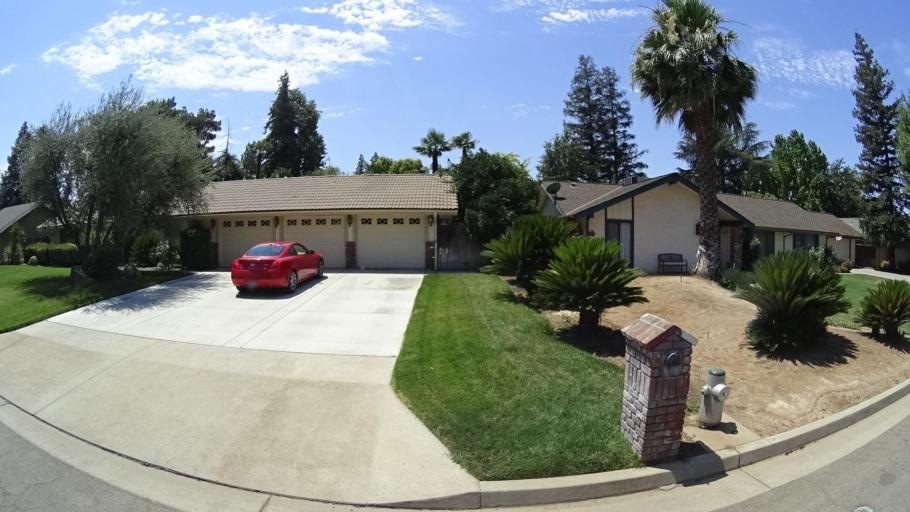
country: US
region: California
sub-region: Fresno County
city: Sunnyside
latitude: 36.7280
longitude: -119.7159
